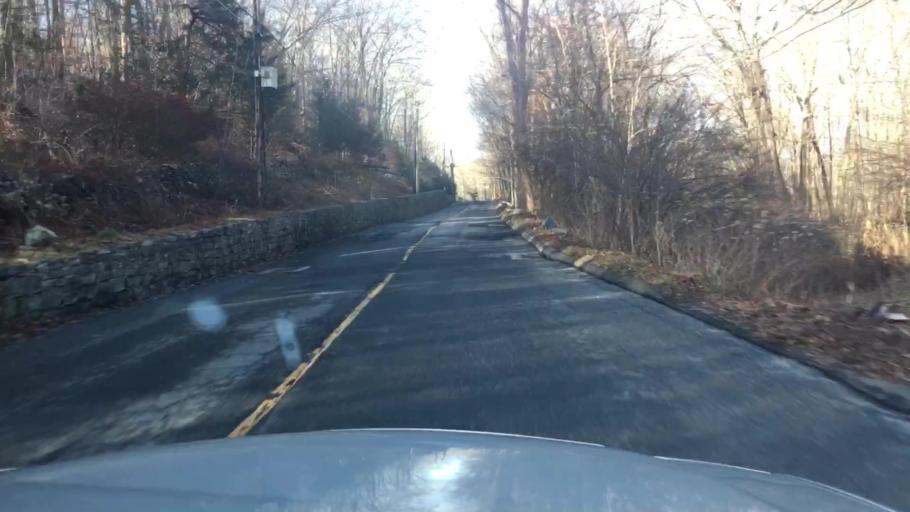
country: US
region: Connecticut
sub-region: Middlesex County
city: Deep River Center
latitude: 41.3802
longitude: -72.4140
